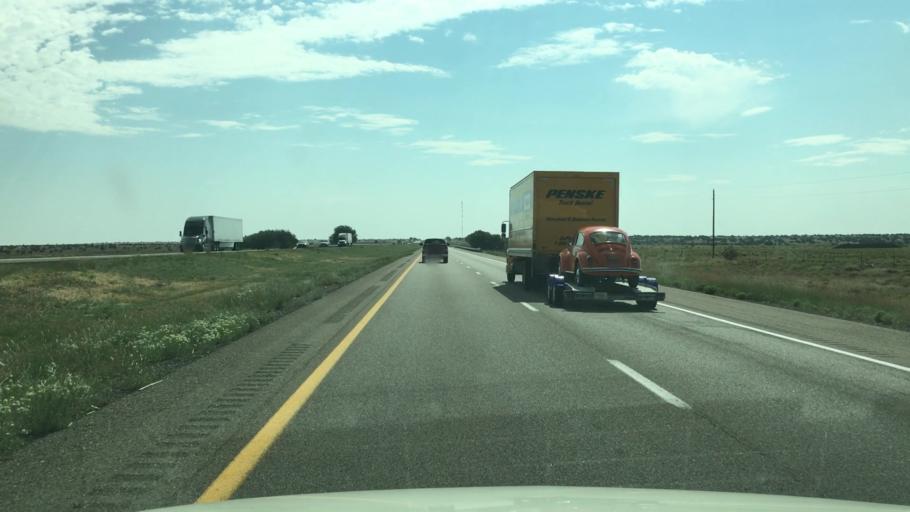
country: US
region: New Mexico
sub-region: Guadalupe County
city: Santa Rosa
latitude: 34.9738
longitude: -104.9419
